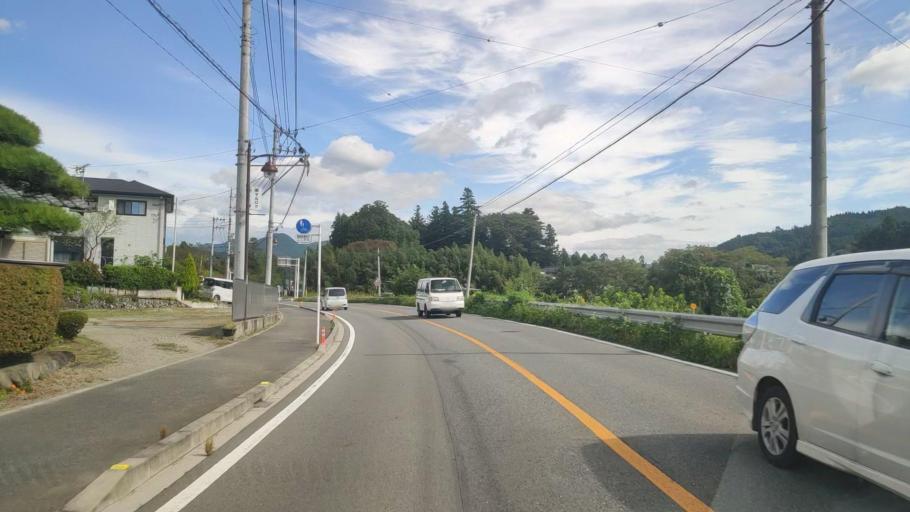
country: JP
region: Gunma
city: Nakanojomachi
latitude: 36.5894
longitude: 138.8603
